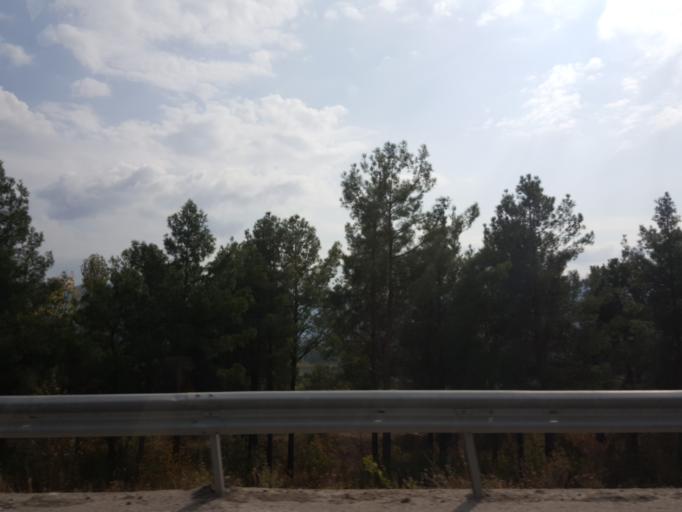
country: TR
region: Corum
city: Hacihamza
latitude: 41.1126
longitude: 34.3967
